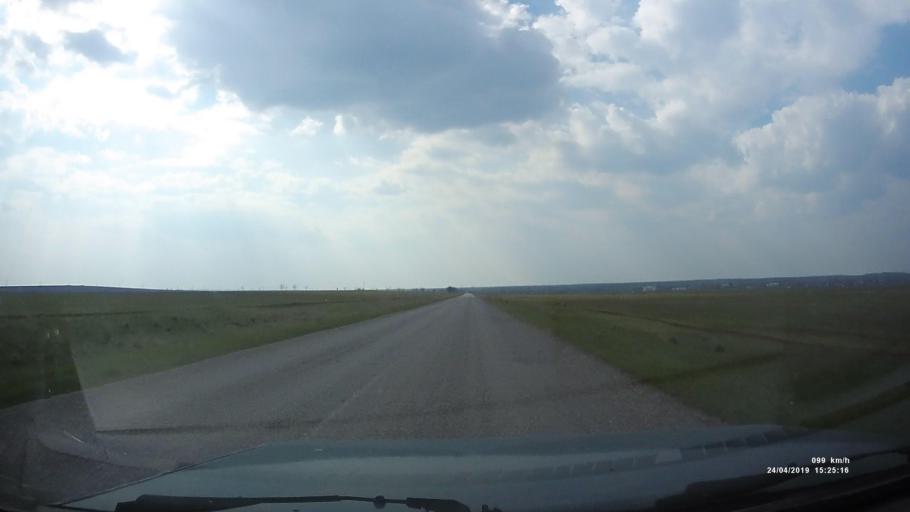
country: RU
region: Rostov
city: Remontnoye
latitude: 46.5516
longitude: 43.0514
